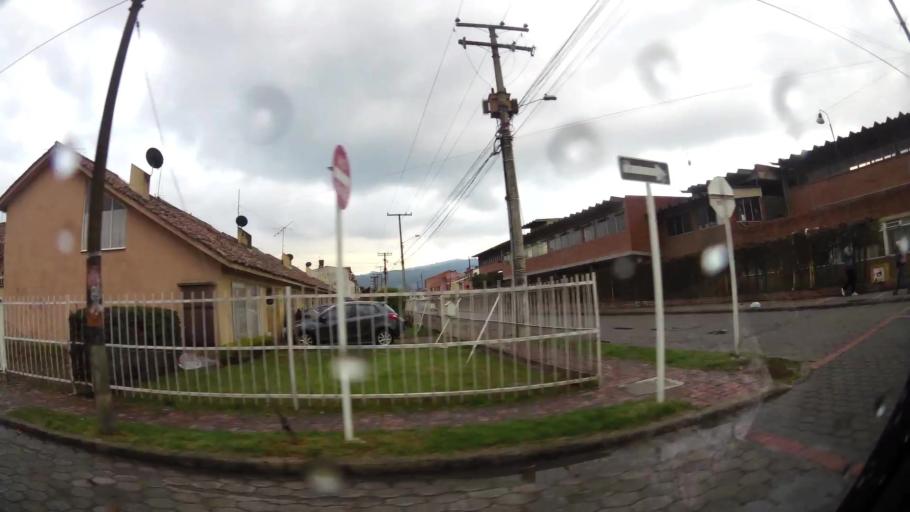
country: CO
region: Cundinamarca
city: Chia
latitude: 4.8662
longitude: -74.0545
